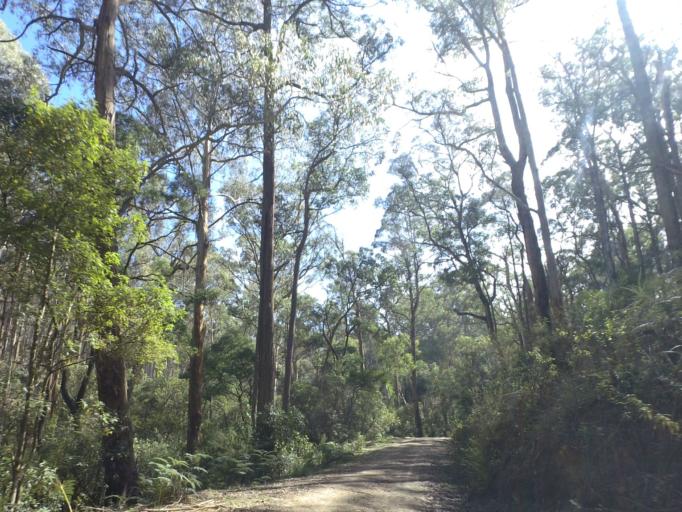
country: AU
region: Victoria
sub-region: Moorabool
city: Bacchus Marsh
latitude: -37.4514
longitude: 144.2628
